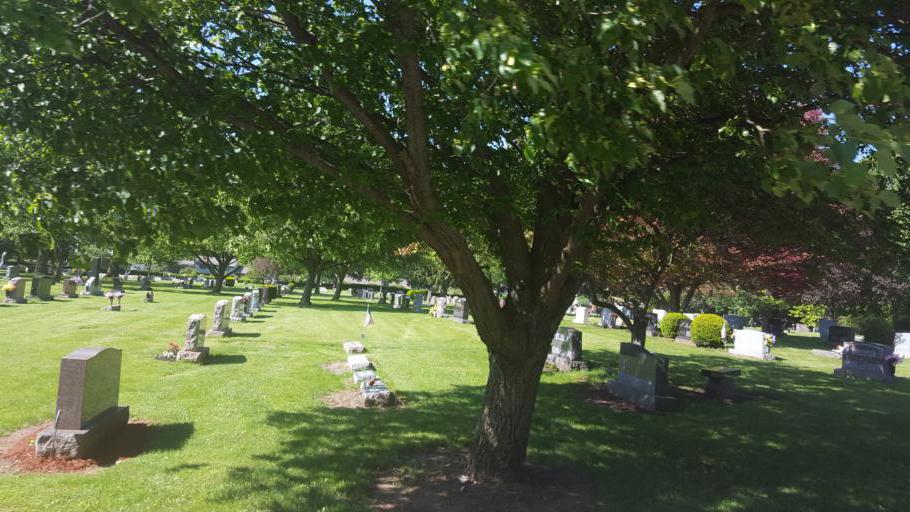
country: US
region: Ohio
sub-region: Marion County
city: Marion
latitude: 40.5730
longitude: -83.1177
